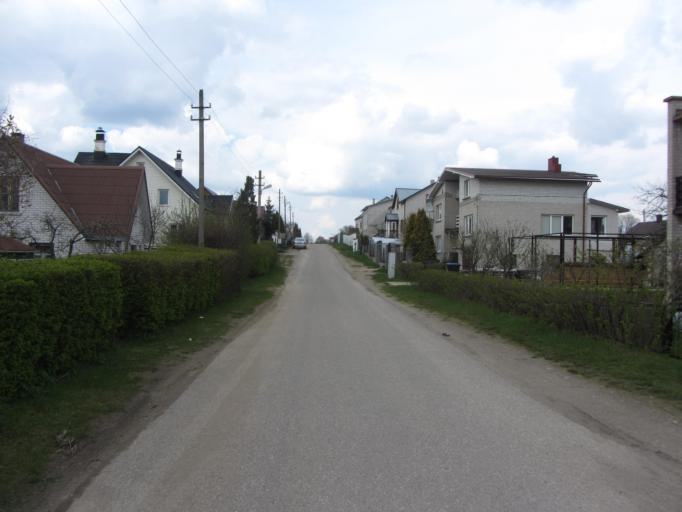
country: LT
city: Lentvaris
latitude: 54.6423
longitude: 25.0434
